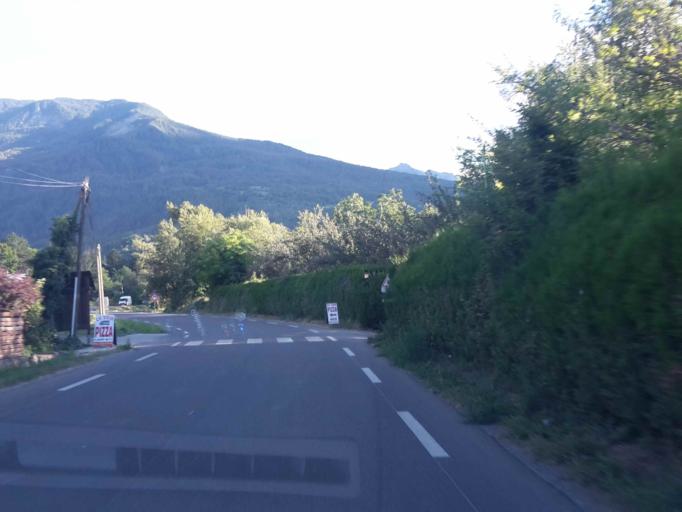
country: FR
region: Provence-Alpes-Cote d'Azur
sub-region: Departement des Hautes-Alpes
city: Embrun
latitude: 44.5450
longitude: 6.4981
